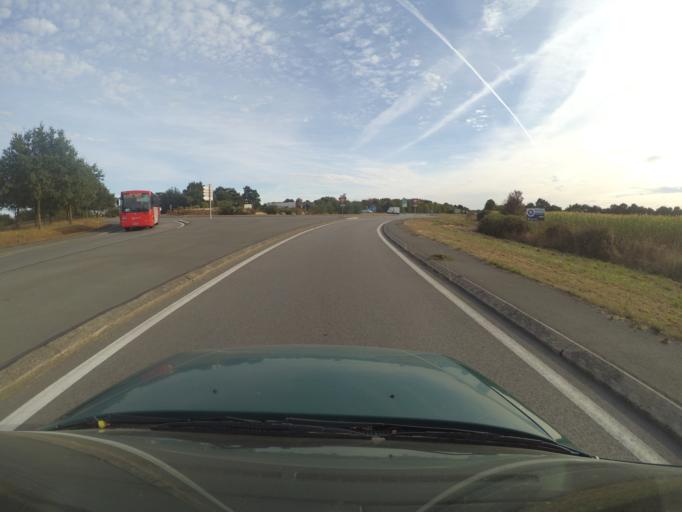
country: FR
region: Pays de la Loire
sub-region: Departement de la Vendee
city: Saint-Hilaire-de-Loulay
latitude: 47.0100
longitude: -1.3384
